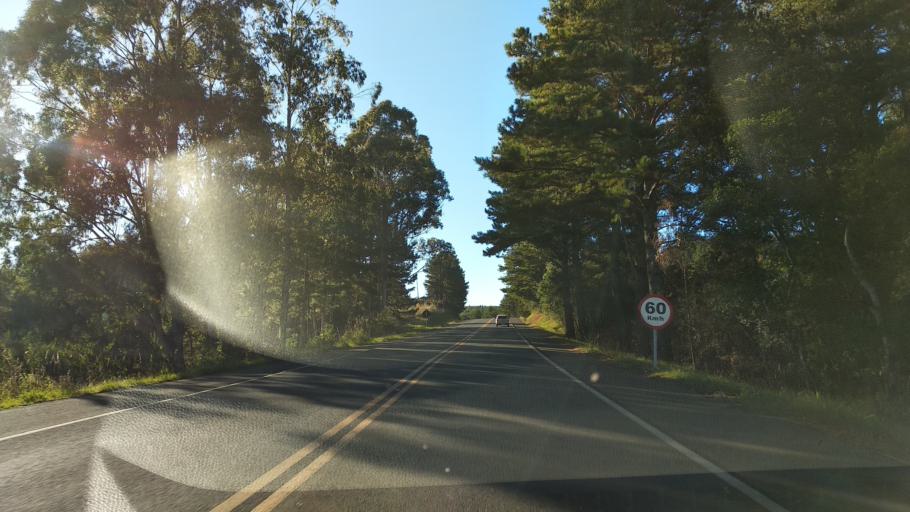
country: BR
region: Santa Catarina
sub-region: Lages
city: Lages
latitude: -27.7858
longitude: -50.4416
